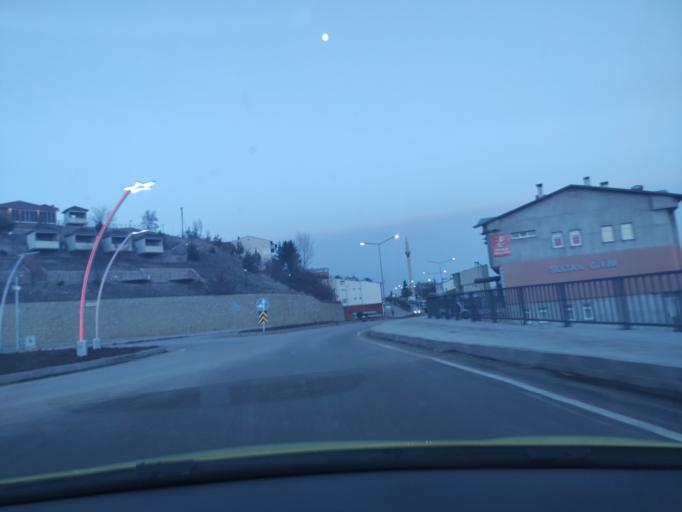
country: TR
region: Bayburt
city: Aydintepe
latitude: 40.3888
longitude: 40.1471
